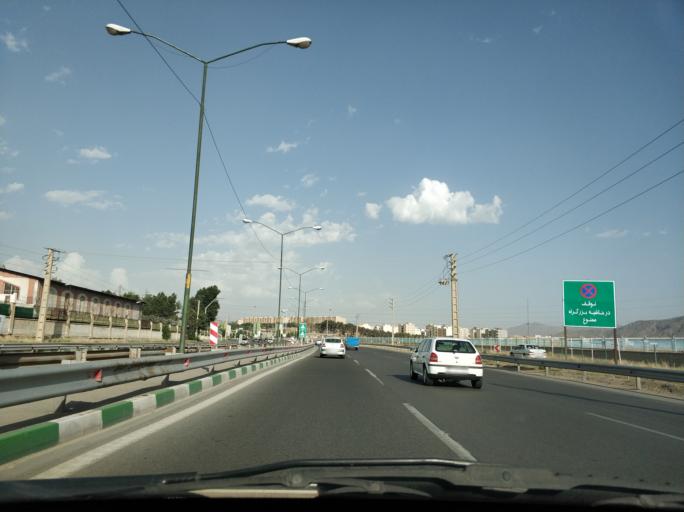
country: IR
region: Tehran
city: Tajrish
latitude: 35.7492
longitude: 51.5855
